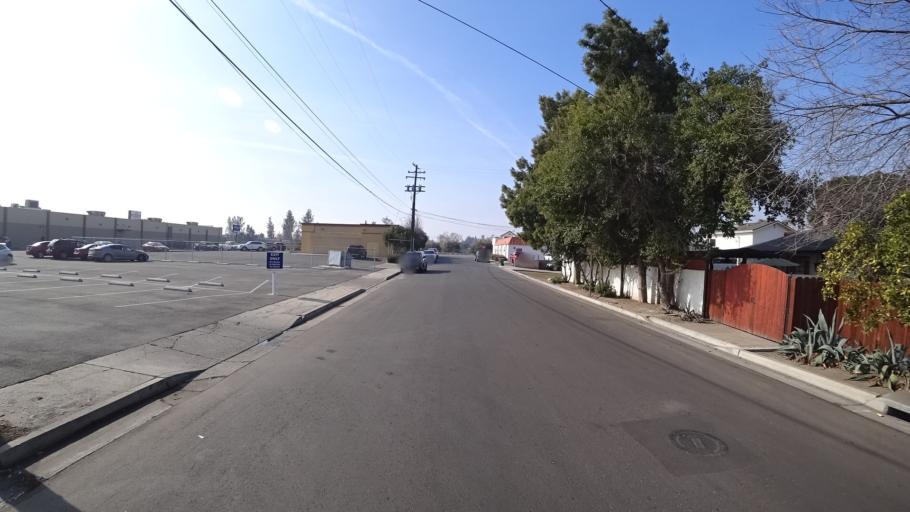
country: US
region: California
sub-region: Kern County
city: Bakersfield
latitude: 35.3561
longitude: -119.0378
